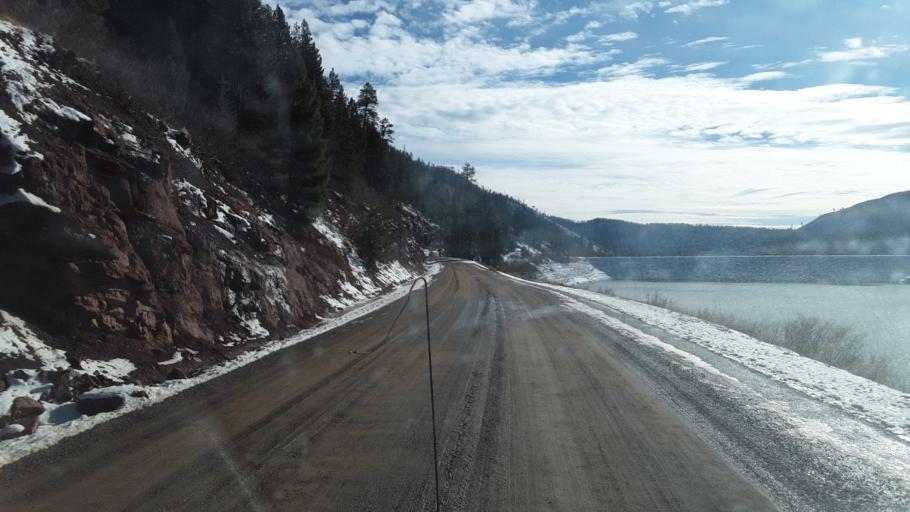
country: US
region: Colorado
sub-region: La Plata County
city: Bayfield
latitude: 37.3895
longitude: -107.6569
